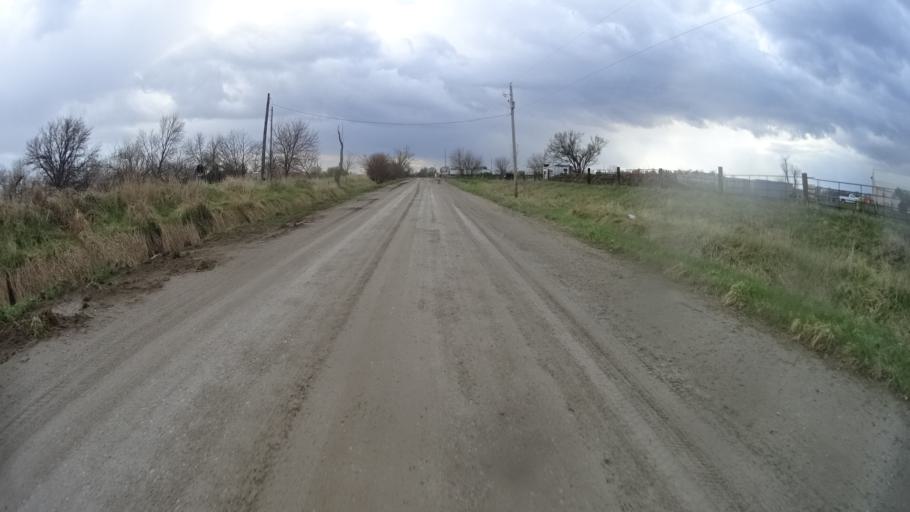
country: US
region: Nebraska
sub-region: Sarpy County
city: Offutt Air Force Base
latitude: 41.0779
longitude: -95.9207
